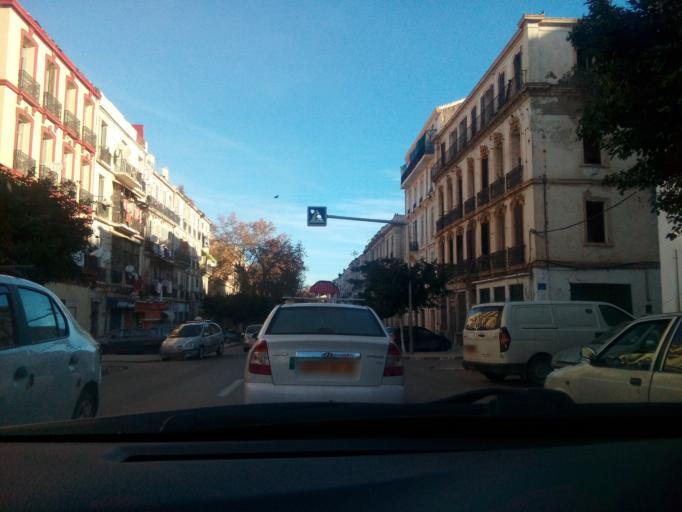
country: DZ
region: Oran
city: Oran
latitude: 35.7024
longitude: -0.6532
